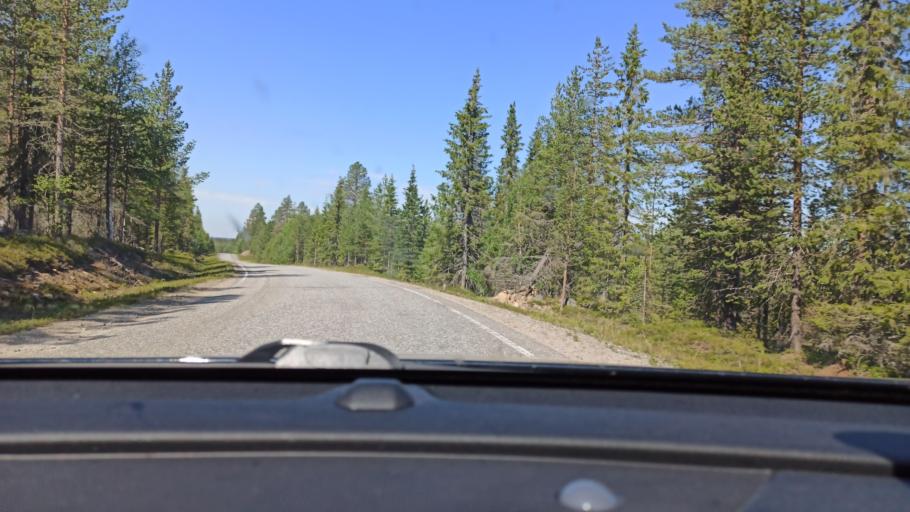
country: FI
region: Lapland
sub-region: Tunturi-Lappi
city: Kolari
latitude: 67.6824
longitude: 24.1358
